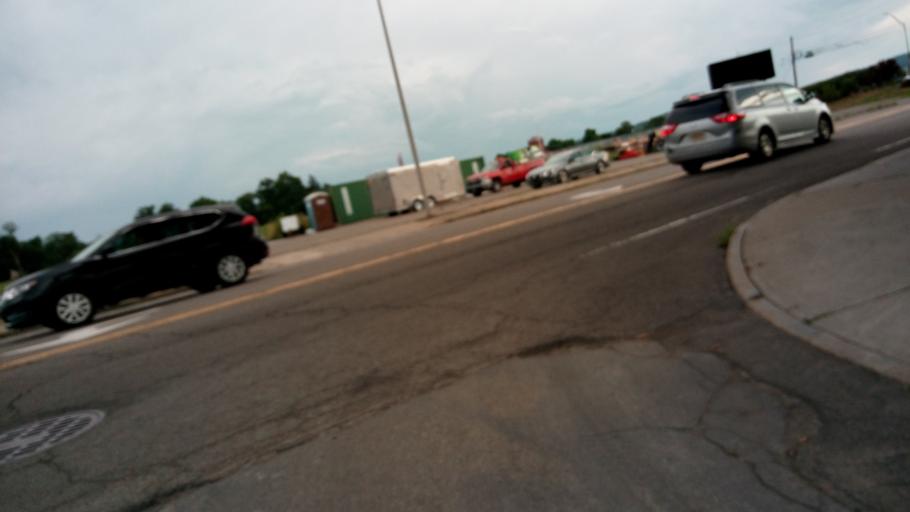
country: US
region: New York
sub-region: Chemung County
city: Elmira
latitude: 42.0889
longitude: -76.7969
